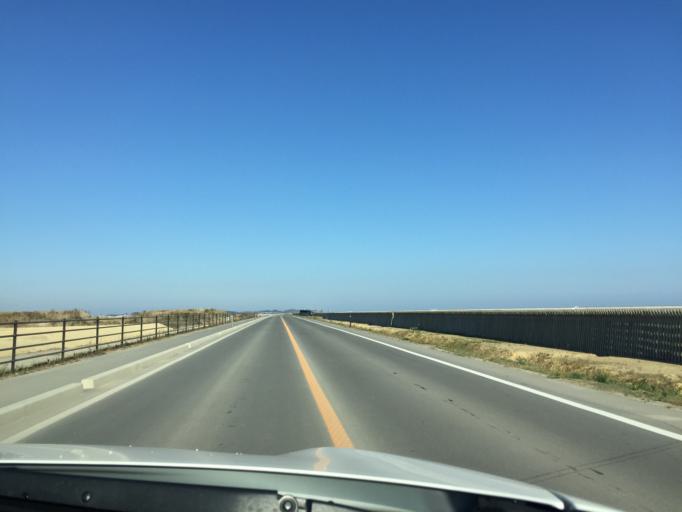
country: JP
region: Miyagi
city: Marumori
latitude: 37.7819
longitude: 140.9842
